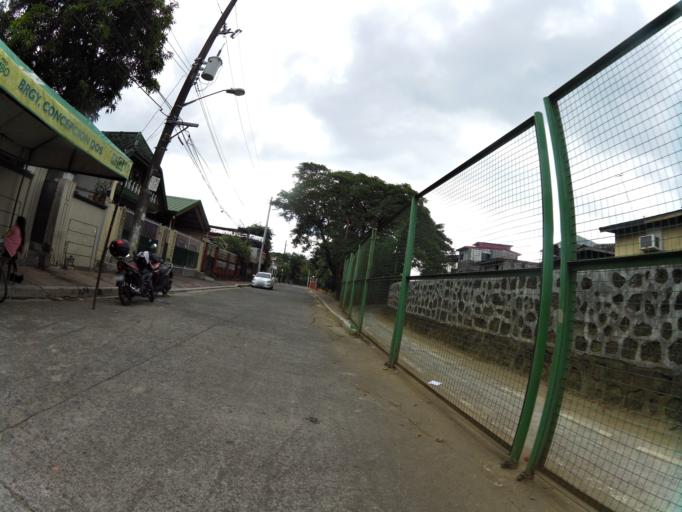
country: PH
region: Calabarzon
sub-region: Province of Rizal
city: Antipolo
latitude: 14.6364
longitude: 121.1099
